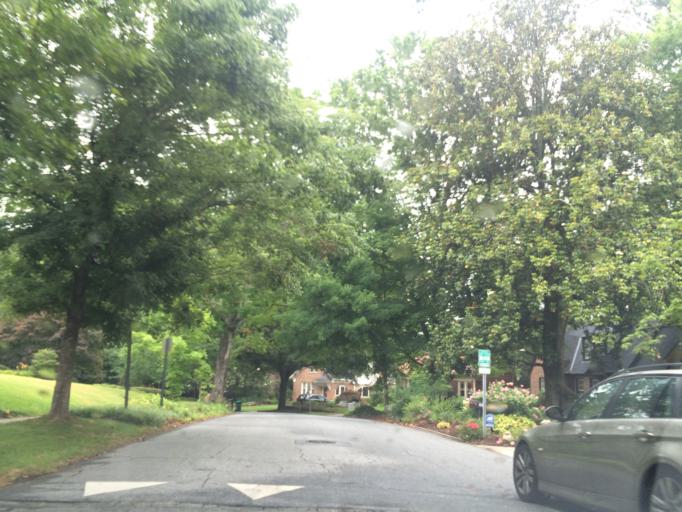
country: US
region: Georgia
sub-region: DeKalb County
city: Druid Hills
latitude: 33.7923
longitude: -84.3295
